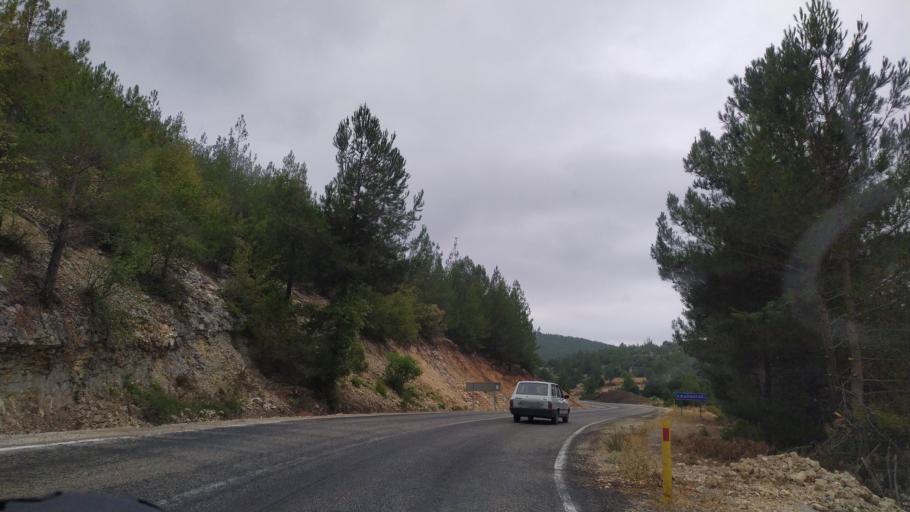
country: TR
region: Mersin
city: Silifke
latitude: 36.5401
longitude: 33.9379
